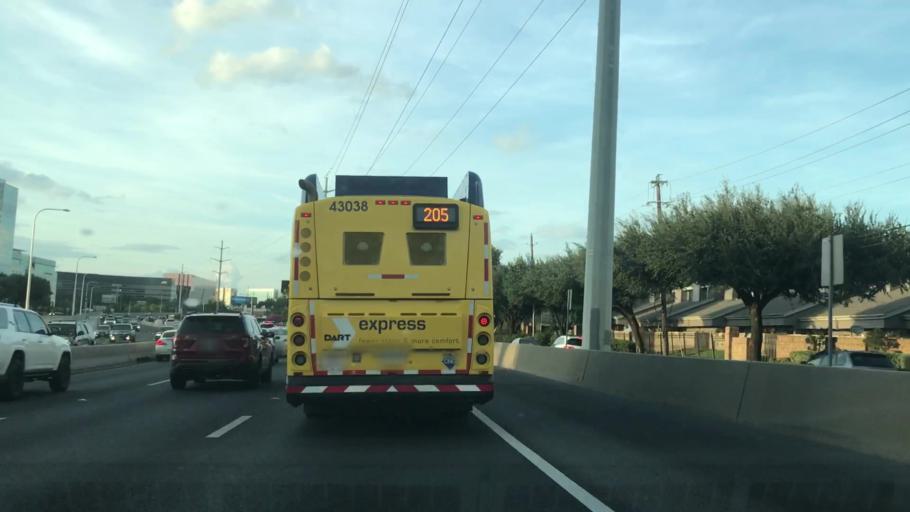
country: US
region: Texas
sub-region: Dallas County
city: Addison
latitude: 32.9419
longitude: -96.8219
